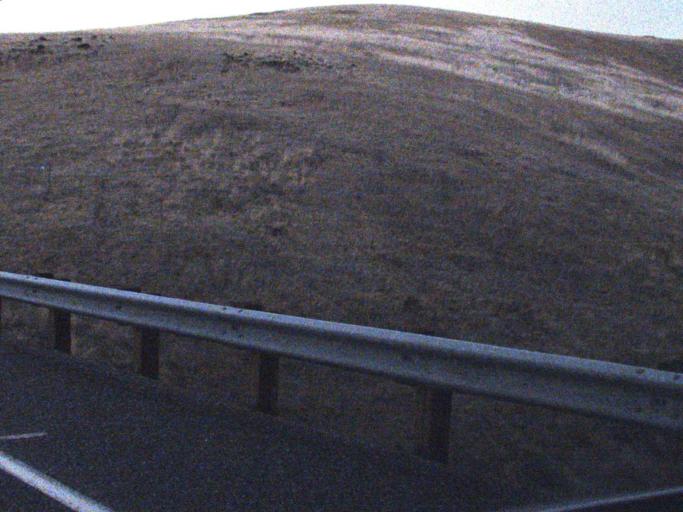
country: US
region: Washington
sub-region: Garfield County
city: Pomeroy
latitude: 46.5644
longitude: -117.7763
